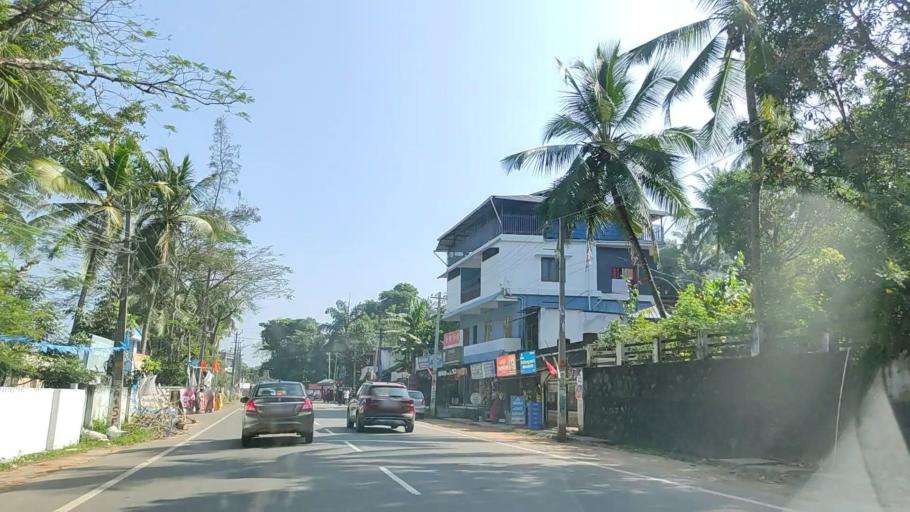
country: IN
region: Kerala
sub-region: Kollam
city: Punalur
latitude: 8.9331
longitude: 76.9405
